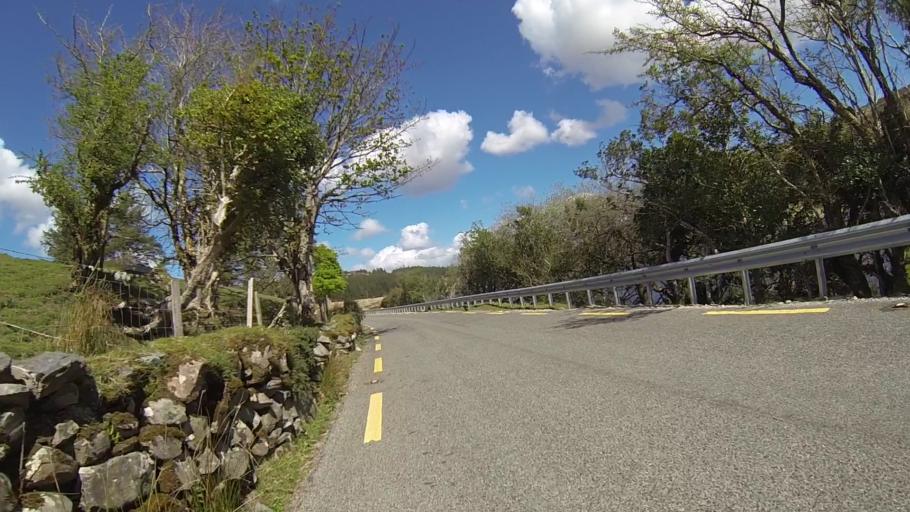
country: IE
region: Munster
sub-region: Ciarrai
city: Kenmare
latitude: 51.9558
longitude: -9.6228
